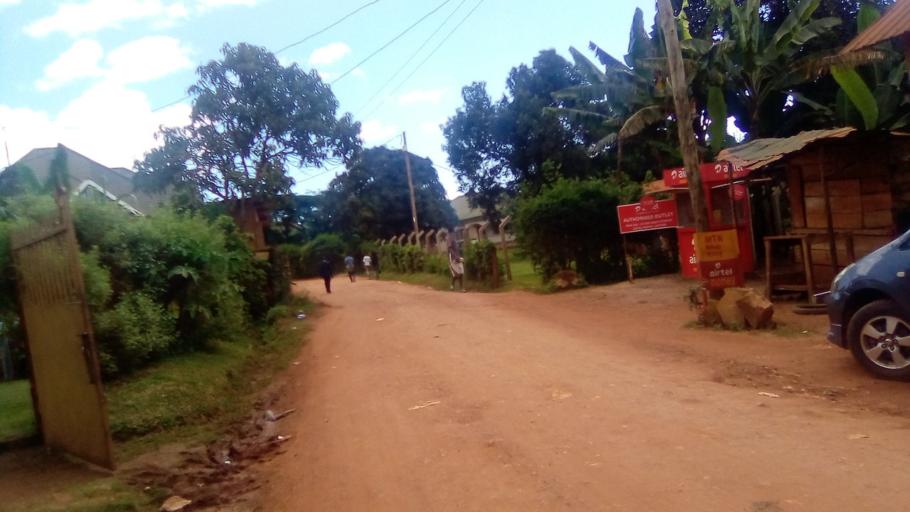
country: UG
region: Central Region
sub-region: Wakiso District
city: Entebbe
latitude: 0.1040
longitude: 32.5243
